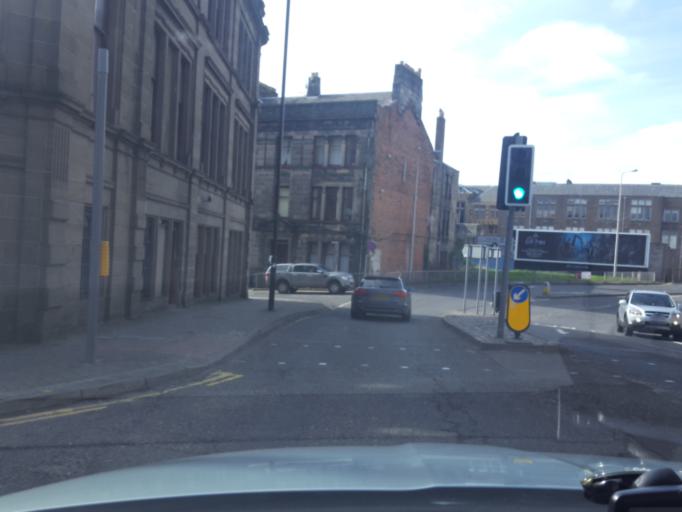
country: GB
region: Scotland
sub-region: Dundee City
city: Dundee
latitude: 56.4643
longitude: -2.9714
